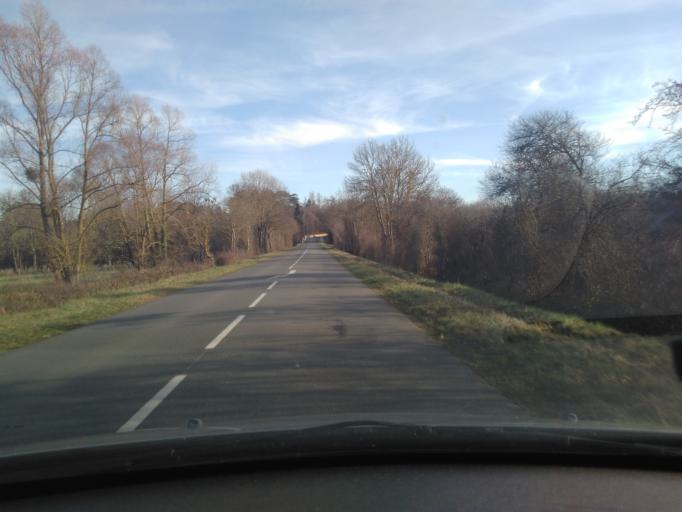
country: FR
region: Centre
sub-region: Departement du Cher
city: Le Chatelet
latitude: 46.6526
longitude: 2.3728
